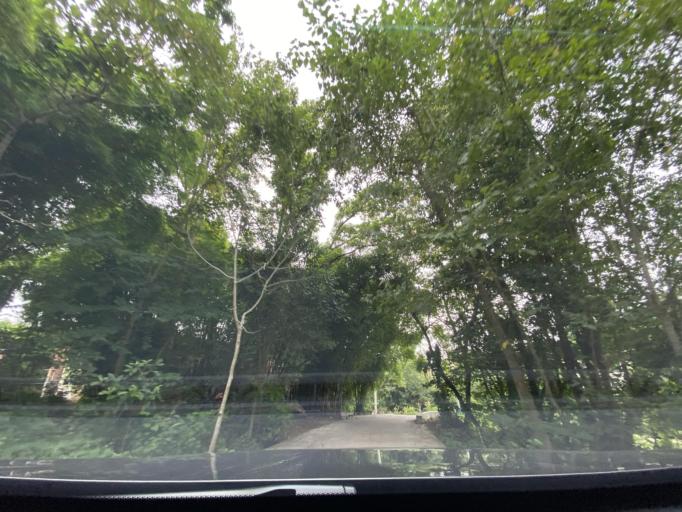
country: CN
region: Sichuan
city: Jiancheng
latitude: 30.3876
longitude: 104.4958
